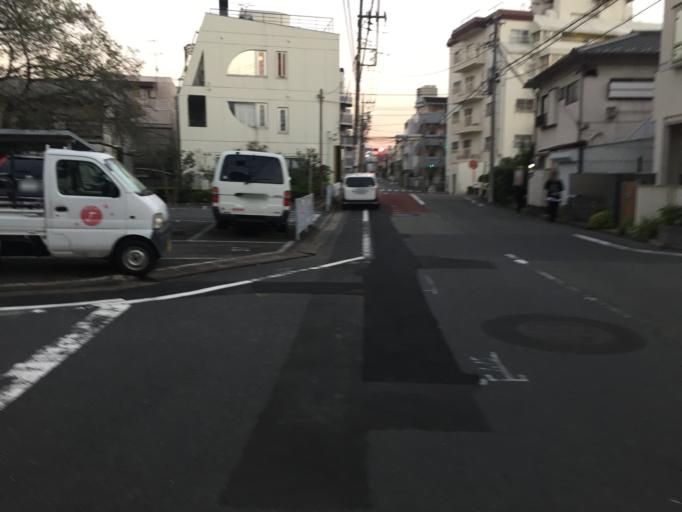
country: JP
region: Tokyo
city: Tokyo
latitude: 35.6387
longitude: 139.6582
